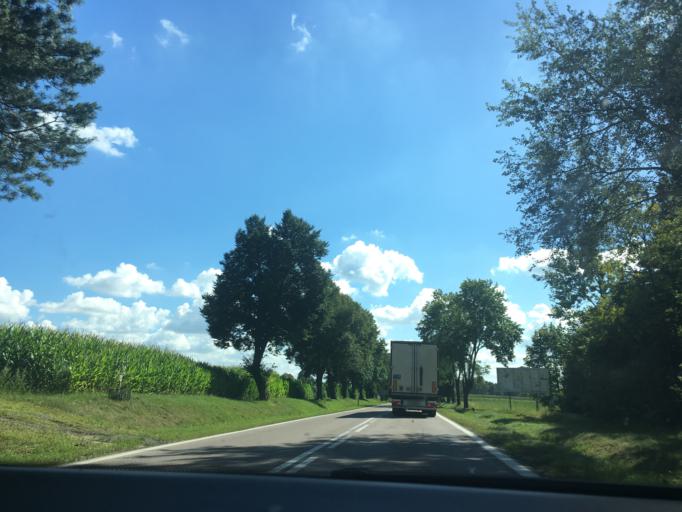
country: PL
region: Podlasie
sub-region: Powiat sokolski
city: Suchowola
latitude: 53.5990
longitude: 23.1124
